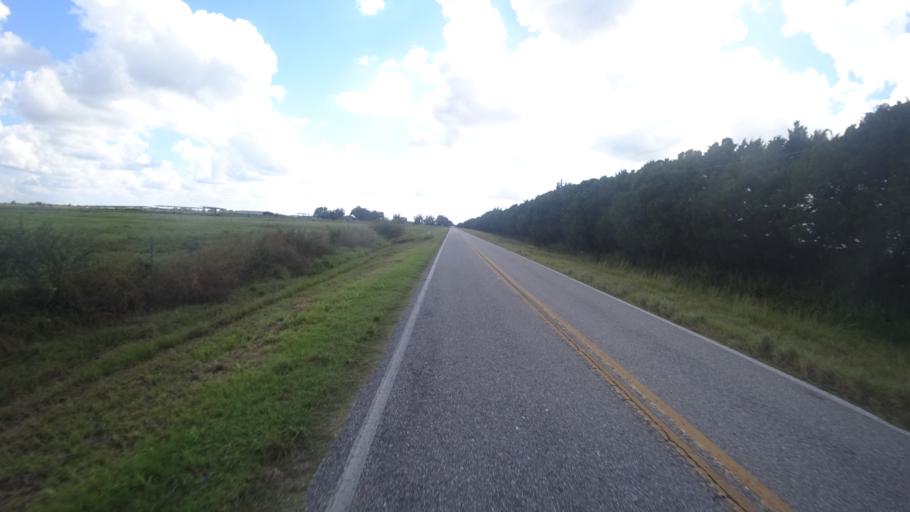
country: US
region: Florida
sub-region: DeSoto County
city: Arcadia
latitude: 27.2948
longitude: -82.1134
